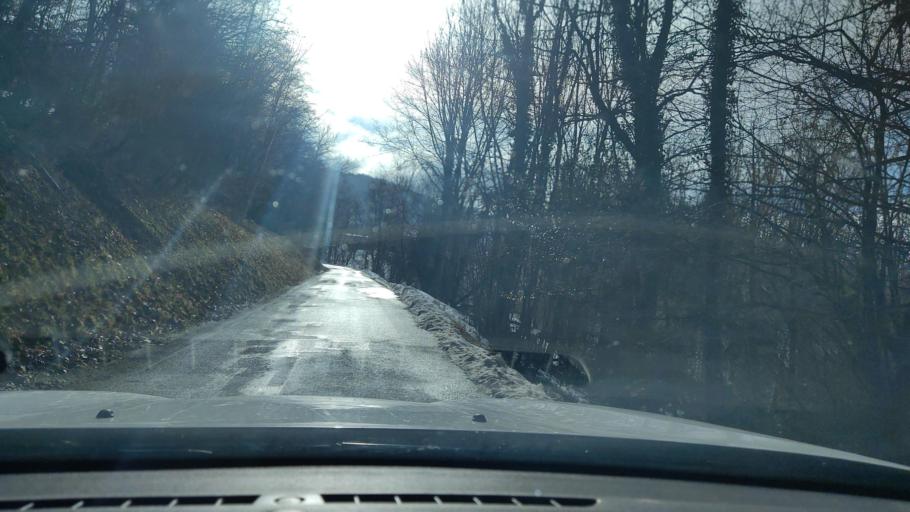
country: FR
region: Rhone-Alpes
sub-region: Departement de la Savoie
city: Marthod
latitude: 45.7020
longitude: 6.4160
